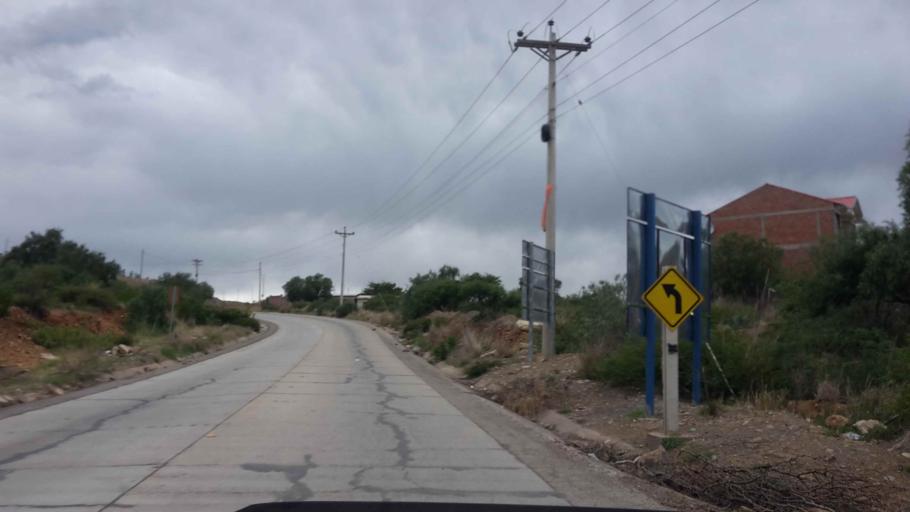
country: BO
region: Cochabamba
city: Cochabamba
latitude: -17.5347
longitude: -66.2049
